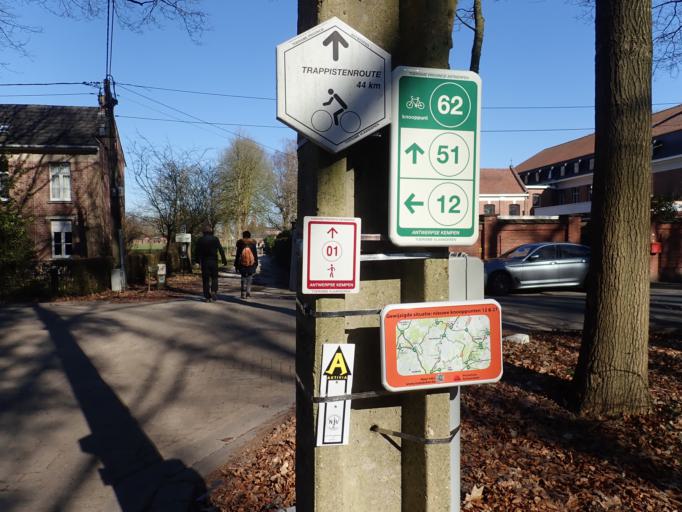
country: BE
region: Flanders
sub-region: Provincie Antwerpen
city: Zoersel
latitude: 51.2803
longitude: 4.6518
